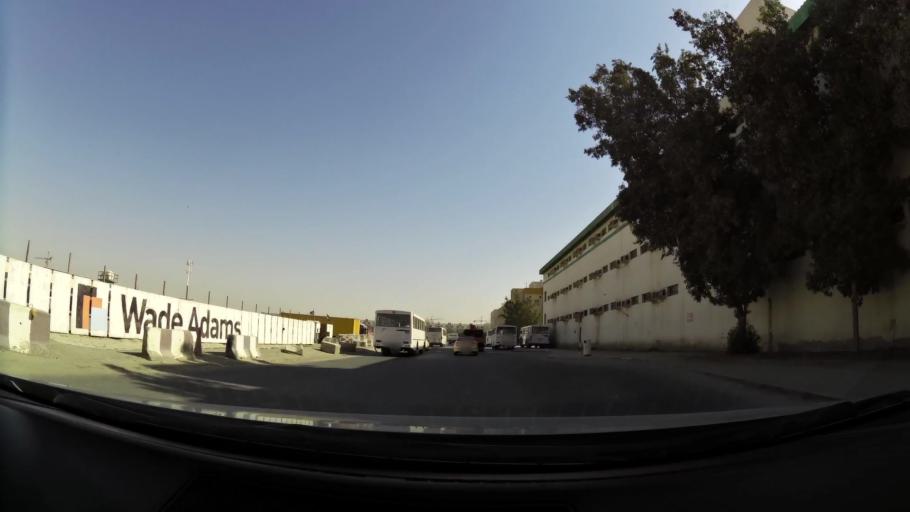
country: AE
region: Dubai
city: Dubai
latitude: 25.0057
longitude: 55.1049
